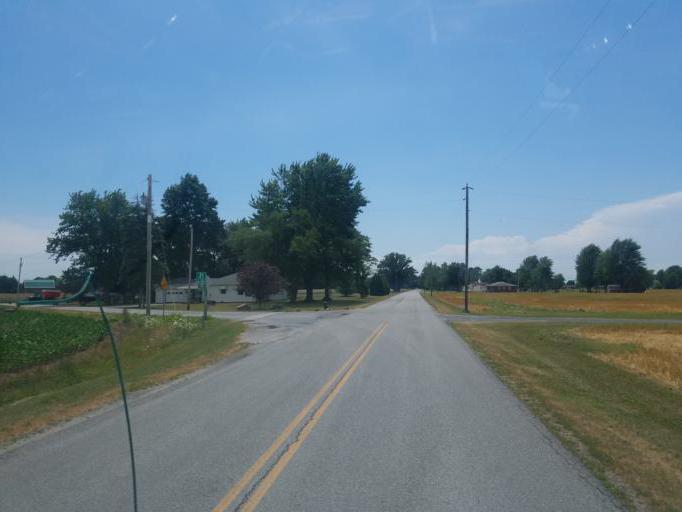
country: US
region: Ohio
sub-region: Paulding County
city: Antwerp
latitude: 41.1949
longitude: -84.7609
